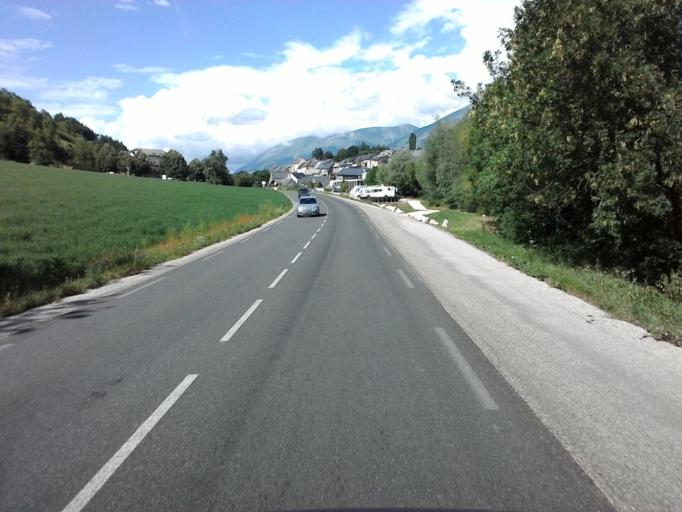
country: FR
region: Rhone-Alpes
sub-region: Departement de l'Isere
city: La Mure
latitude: 44.9044
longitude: 5.7821
